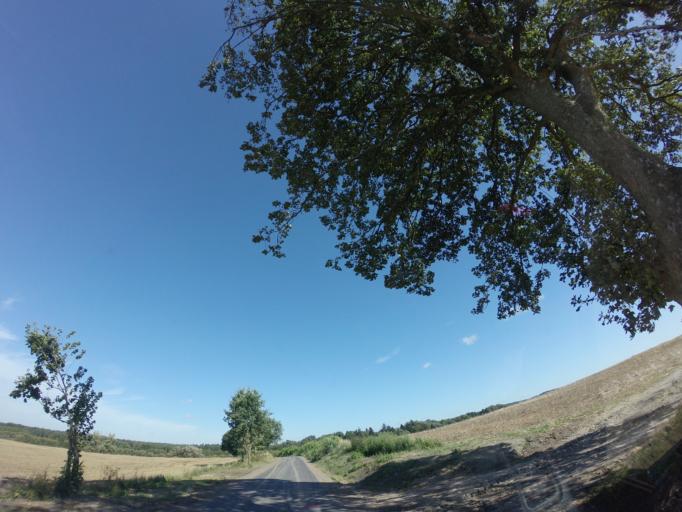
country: PL
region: West Pomeranian Voivodeship
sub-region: Powiat choszczenski
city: Choszczno
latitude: 53.1802
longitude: 15.4999
